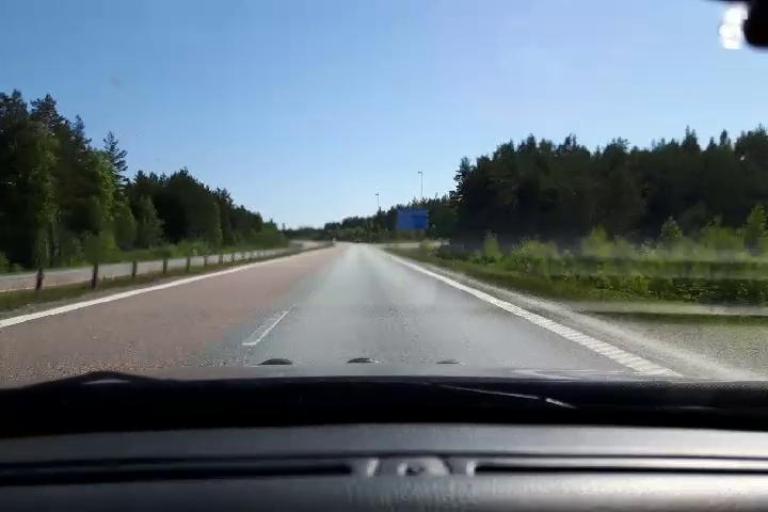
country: SE
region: Gaevleborg
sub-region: Soderhamns Kommun
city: Soderhamn
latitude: 61.3422
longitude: 17.0179
